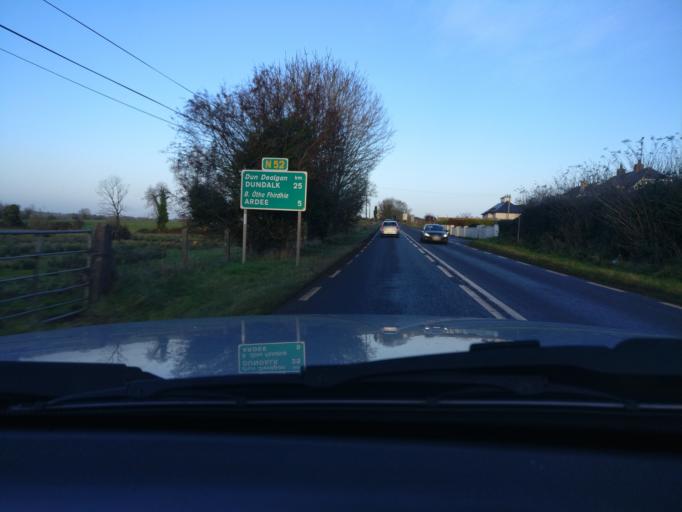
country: IE
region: Leinster
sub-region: Lu
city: Ardee
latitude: 53.8451
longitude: -6.6024
